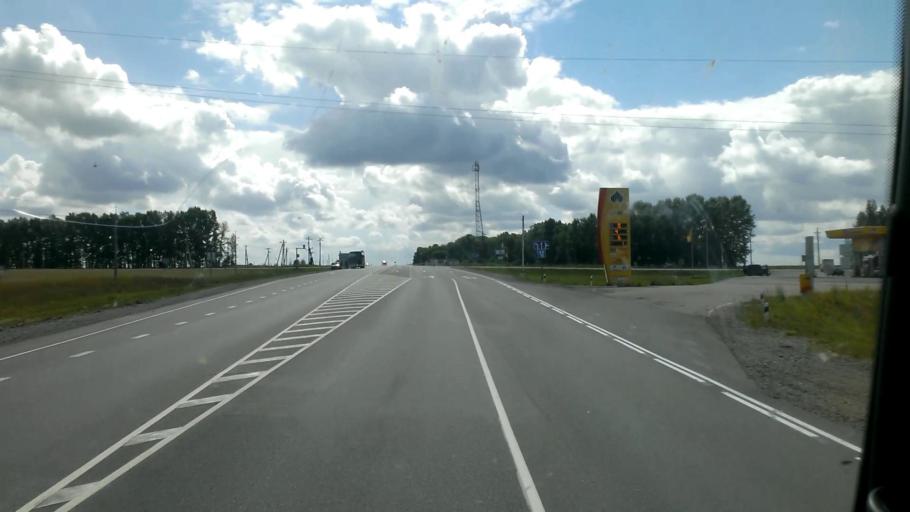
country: RU
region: Altai Krai
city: Troitskoye
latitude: 52.9688
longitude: 84.7497
